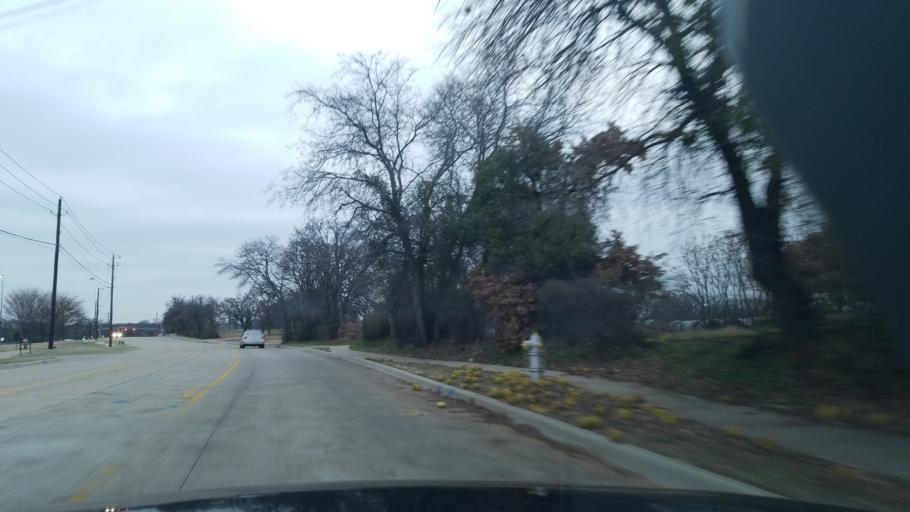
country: US
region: Texas
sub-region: Denton County
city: Corinth
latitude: 33.1328
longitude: -97.0632
